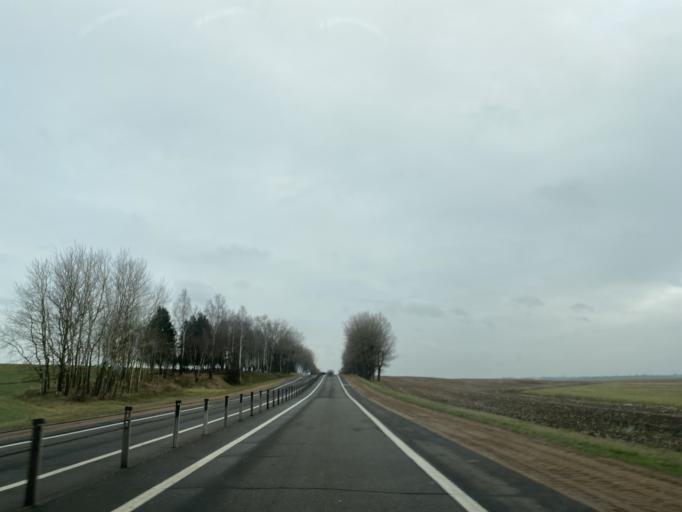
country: BY
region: Minsk
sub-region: Smalyavitski Rayon
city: Usjazh
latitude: 54.0313
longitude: 28.0021
